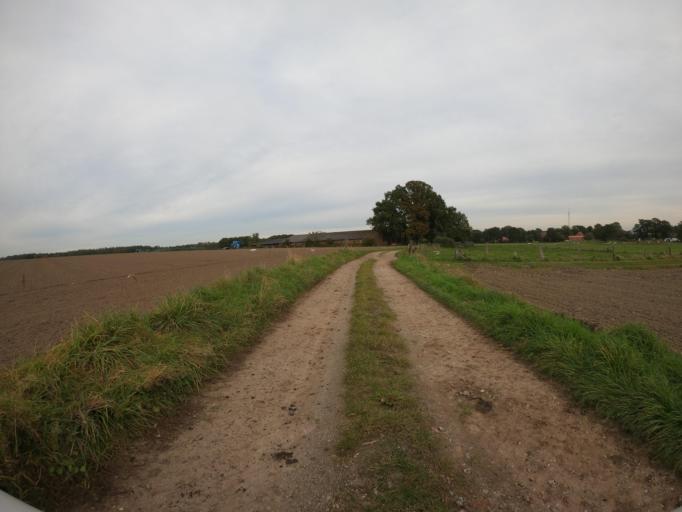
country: DE
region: North Rhine-Westphalia
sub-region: Regierungsbezirk Dusseldorf
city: Schermbeck
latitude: 51.6931
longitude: 6.8963
